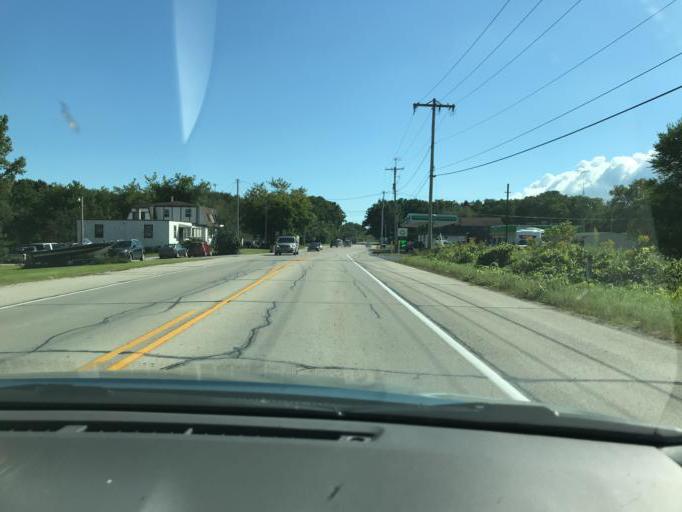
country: US
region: Illinois
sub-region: Lake County
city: Winthrop Harbor
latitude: 42.4944
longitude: -87.8220
